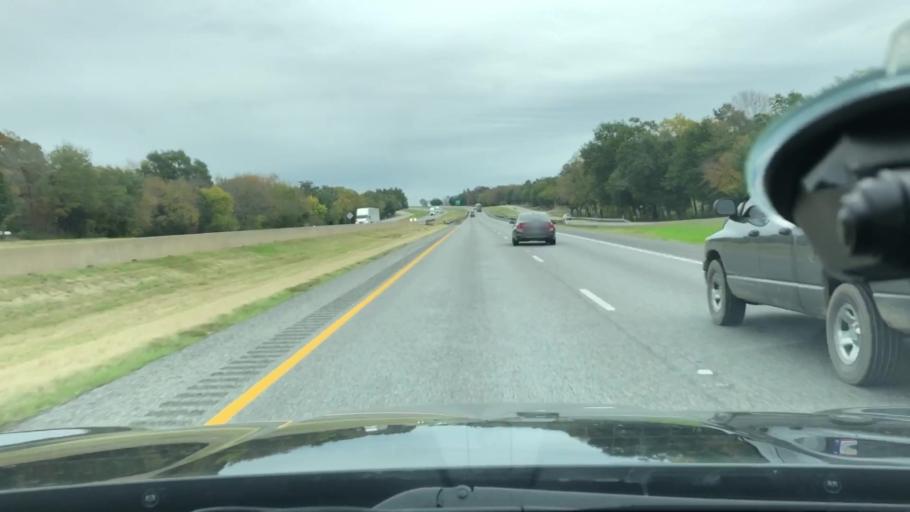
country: US
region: Texas
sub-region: Hunt County
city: Greenville
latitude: 33.1289
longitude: -95.9799
